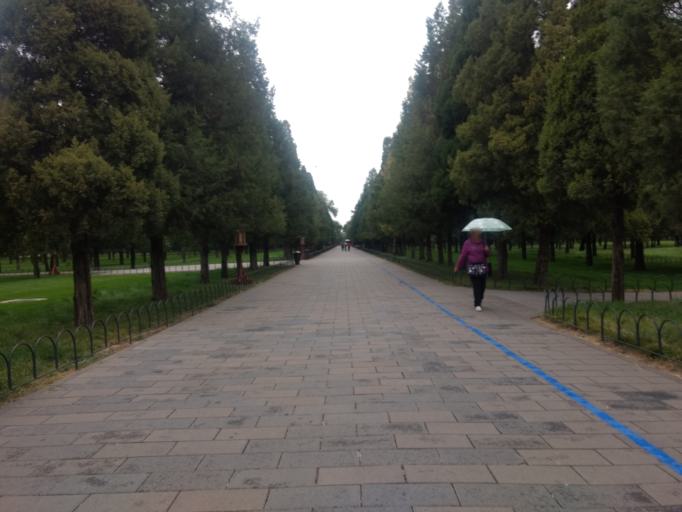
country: CN
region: Beijing
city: Longtan
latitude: 39.8770
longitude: 116.4030
